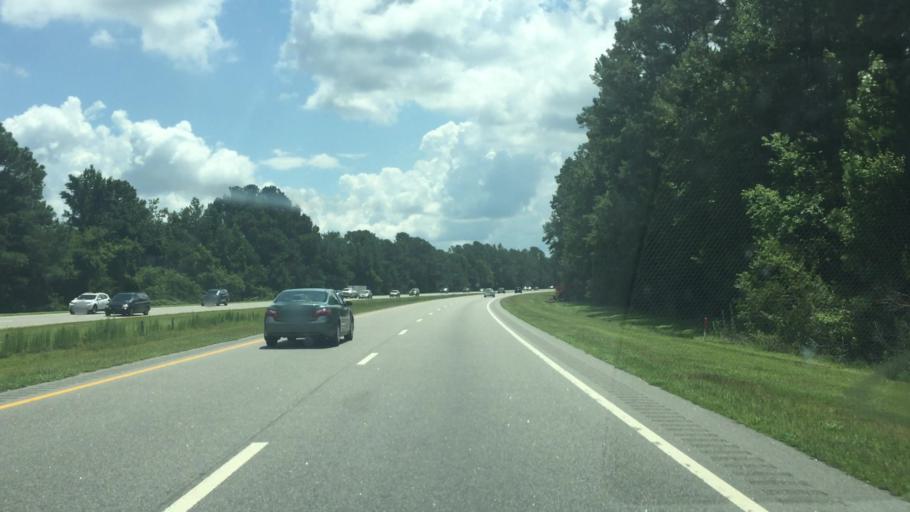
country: US
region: North Carolina
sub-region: Robeson County
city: Lumberton
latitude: 34.5718
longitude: -79.0342
